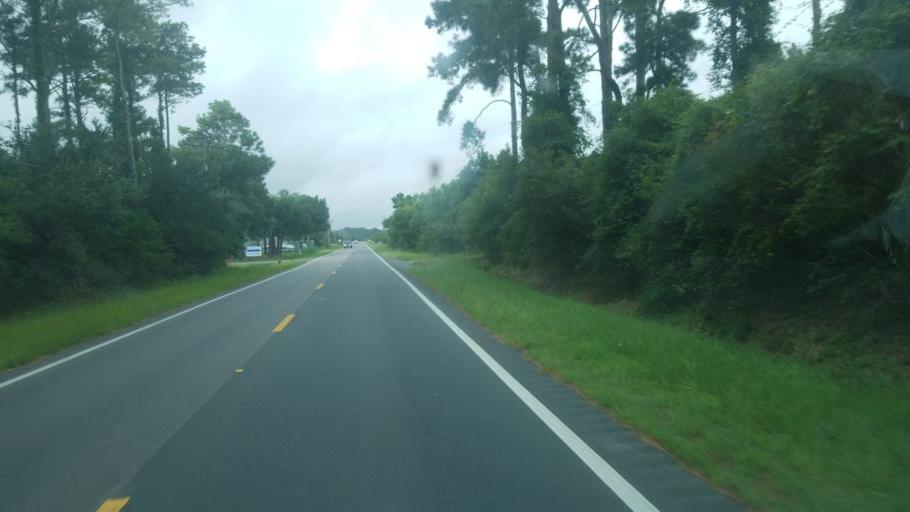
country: US
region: North Carolina
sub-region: Dare County
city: Wanchese
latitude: 35.8628
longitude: -75.6480
